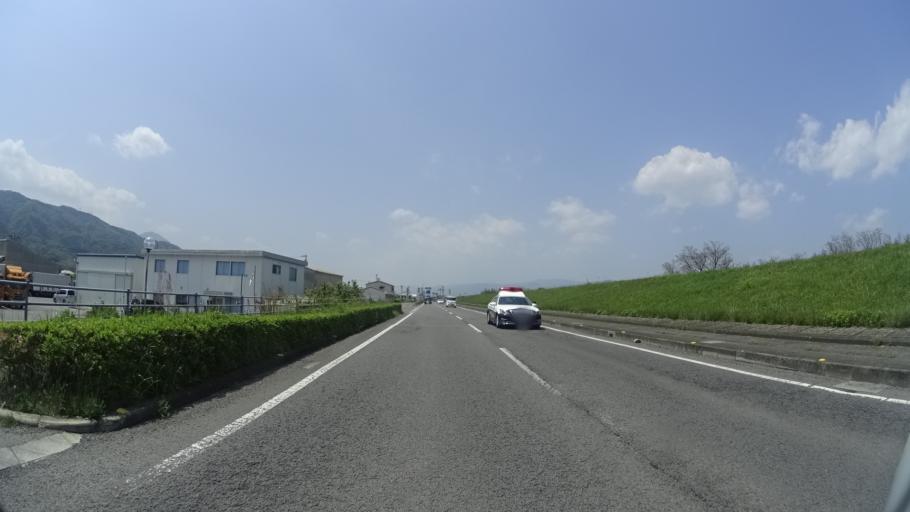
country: JP
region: Tokushima
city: Kamojimacho-jogejima
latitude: 34.0627
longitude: 134.2885
